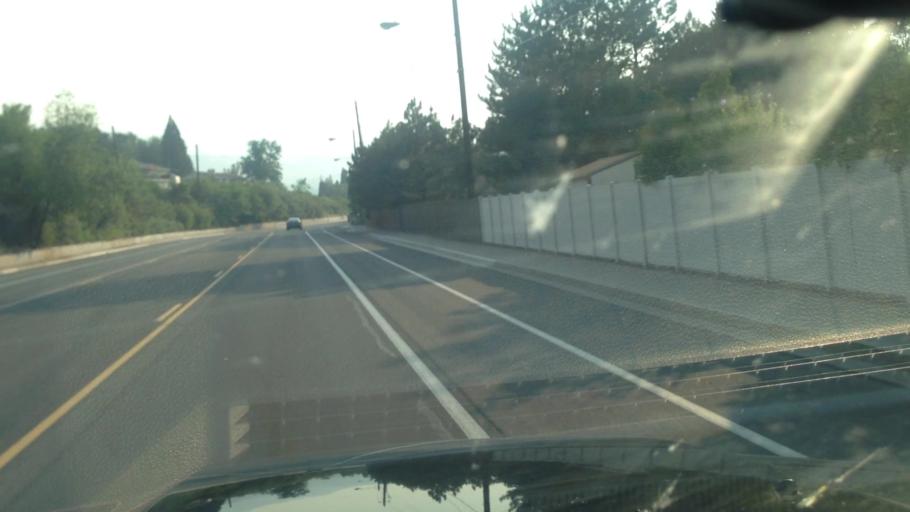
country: US
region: Nevada
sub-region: Washoe County
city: Reno
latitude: 39.5077
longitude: -119.8433
